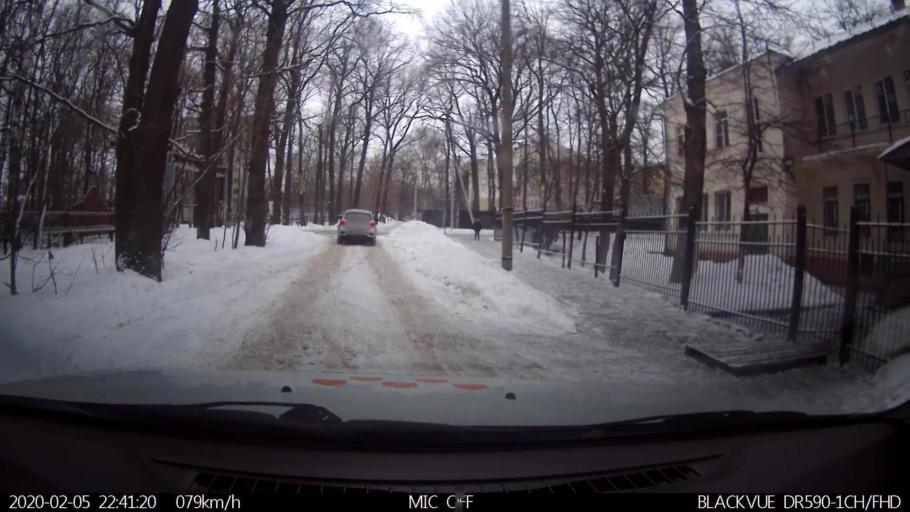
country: RU
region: Nizjnij Novgorod
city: Imeni Stepana Razina
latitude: 54.7208
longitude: 44.3374
